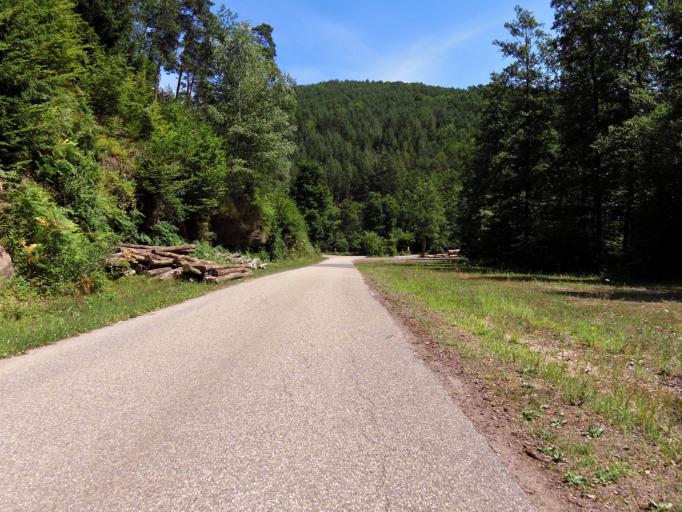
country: DE
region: Rheinland-Pfalz
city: Wilgartswiesen
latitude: 49.2424
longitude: 7.8966
